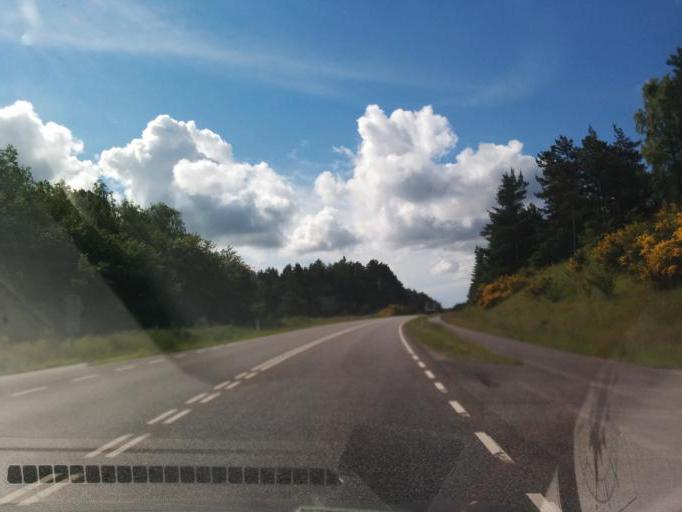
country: DK
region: Central Jutland
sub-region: Syddjurs Kommune
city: Ebeltoft
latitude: 56.2400
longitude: 10.6571
